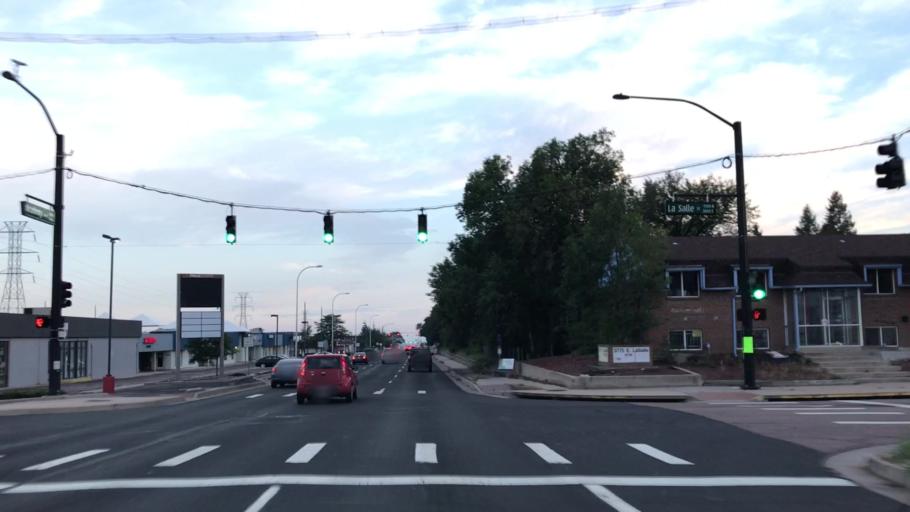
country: US
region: Colorado
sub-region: El Paso County
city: Cimarron Hills
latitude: 38.8574
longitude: -104.7574
